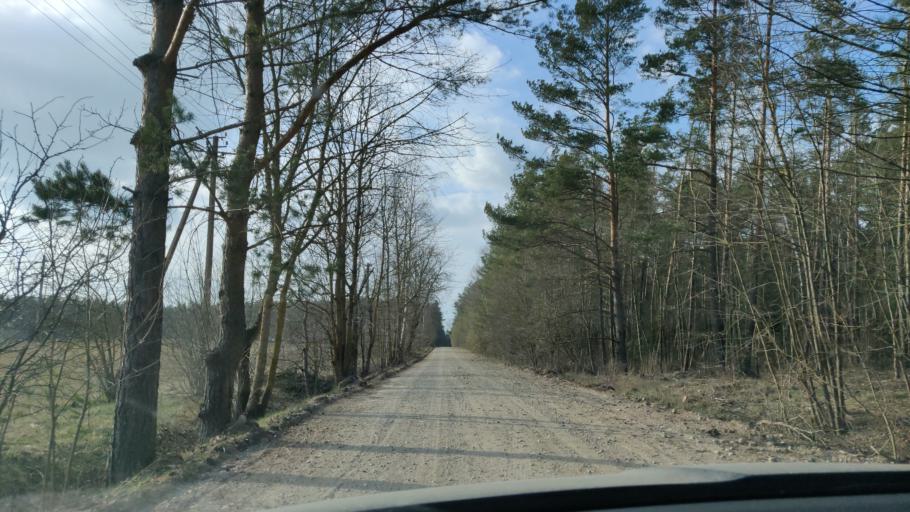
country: LT
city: Lentvaris
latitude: 54.5951
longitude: 25.0845
